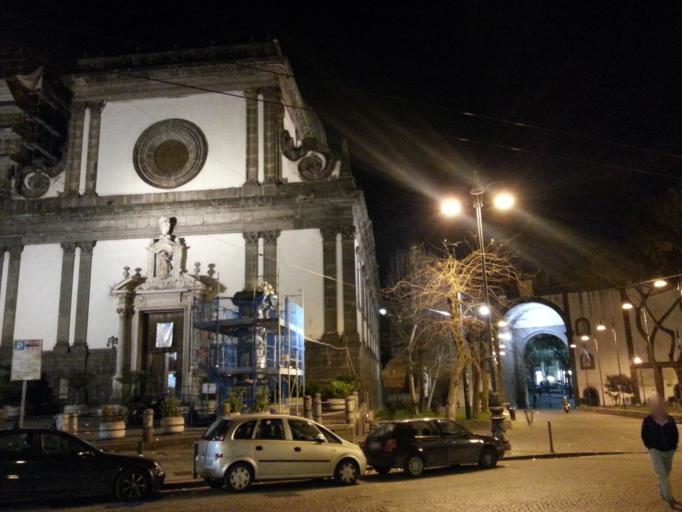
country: IT
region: Campania
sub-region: Provincia di Napoli
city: Napoli
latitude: 40.8542
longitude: 14.2646
